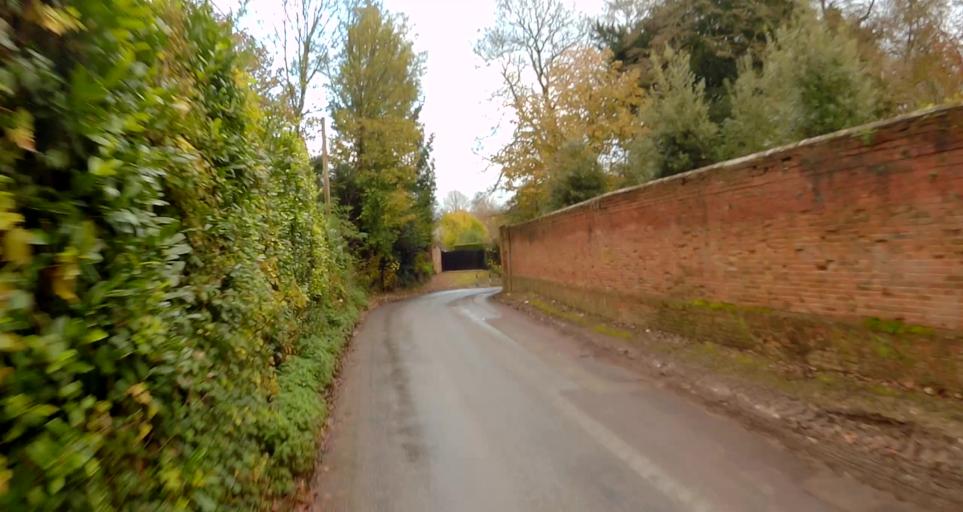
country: GB
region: England
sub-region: Hampshire
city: Old Basing
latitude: 51.2325
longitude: -1.0049
